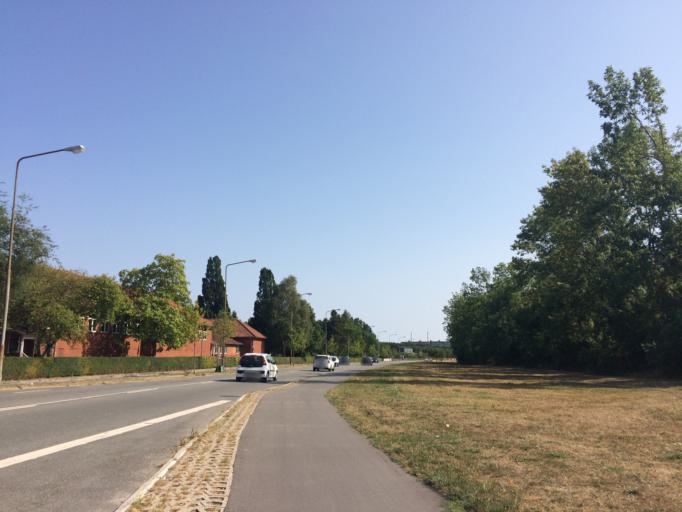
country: DK
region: Capital Region
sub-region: Hvidovre Kommune
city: Hvidovre
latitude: 55.6323
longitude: 12.4536
